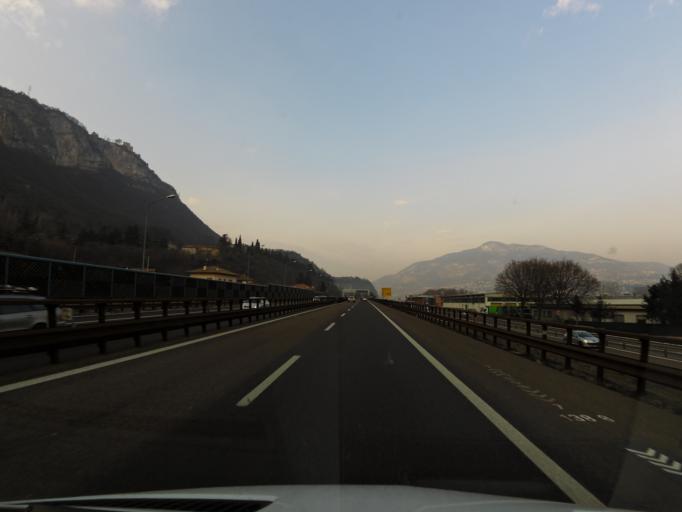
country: IT
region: Trentino-Alto Adige
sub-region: Provincia di Trento
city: Trento
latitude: 46.0573
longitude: 11.1093
